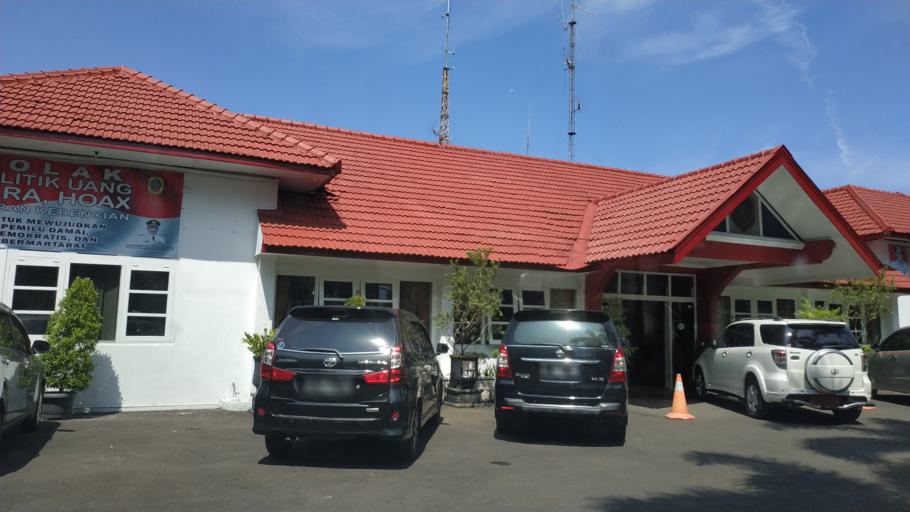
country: ID
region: Central Java
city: Puri
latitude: -6.7513
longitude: 111.0318
